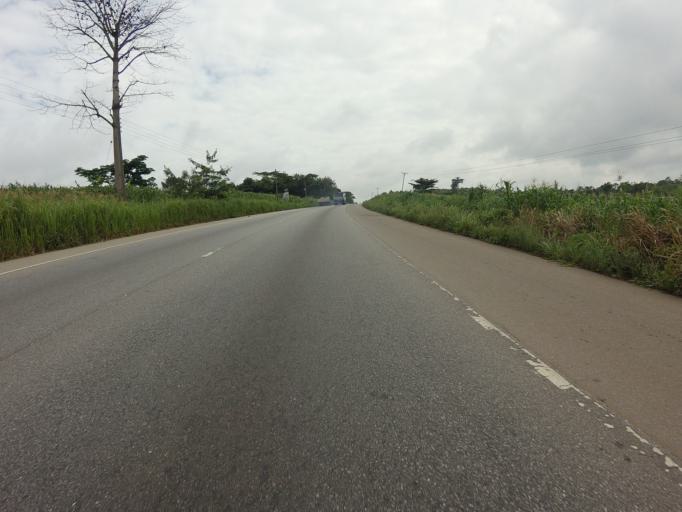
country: GH
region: Ashanti
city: Tafo
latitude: 6.9745
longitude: -1.6858
